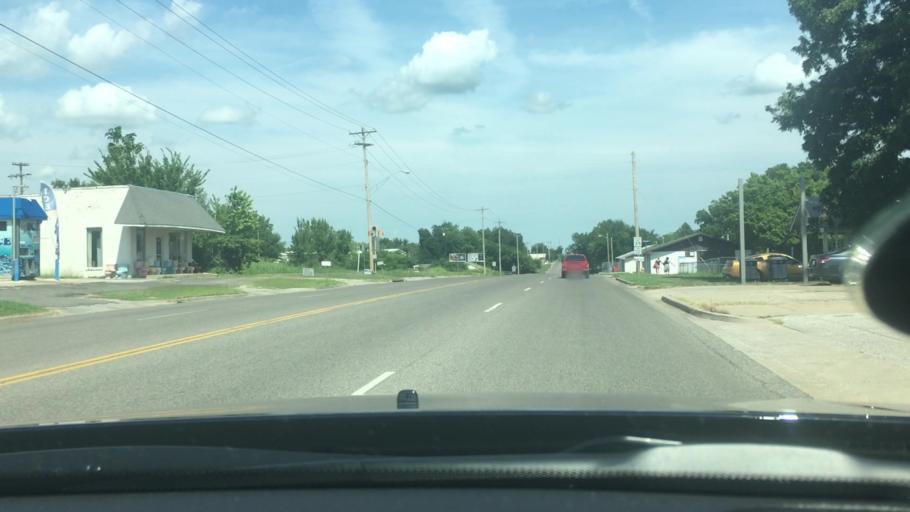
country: US
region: Oklahoma
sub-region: Pottawatomie County
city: Shawnee
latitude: 35.3327
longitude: -96.9043
